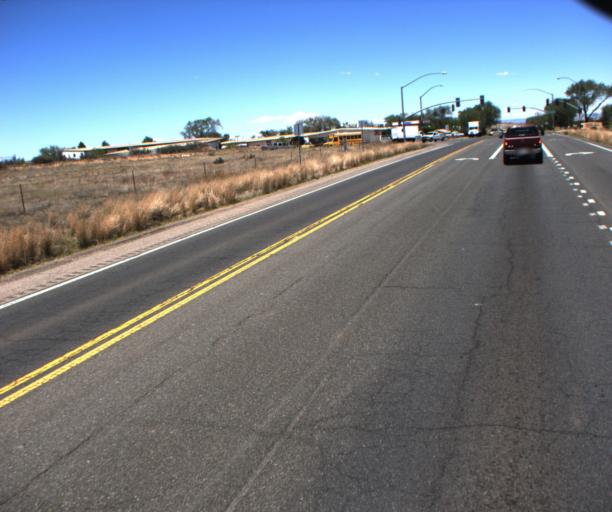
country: US
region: Arizona
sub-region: Yavapai County
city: Prescott
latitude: 34.6428
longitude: -112.4321
